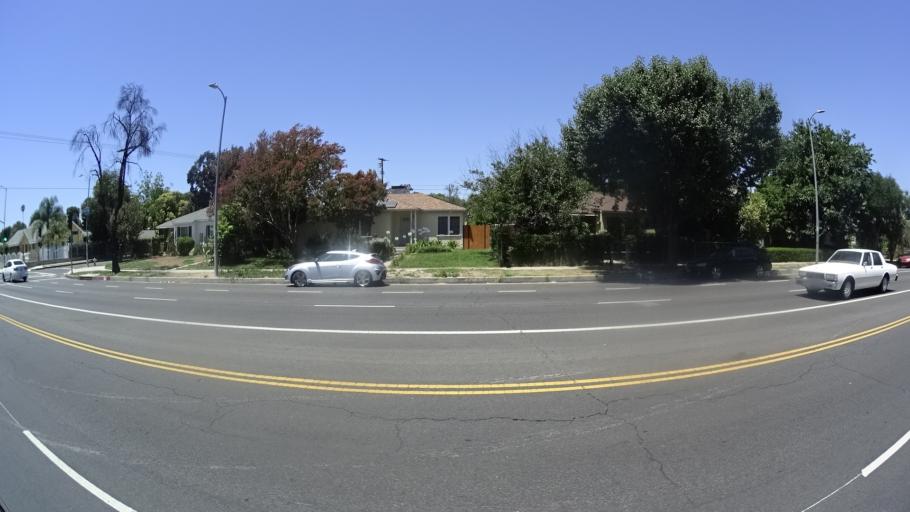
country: US
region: California
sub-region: Los Angeles County
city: Northridge
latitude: 34.1978
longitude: -118.5186
